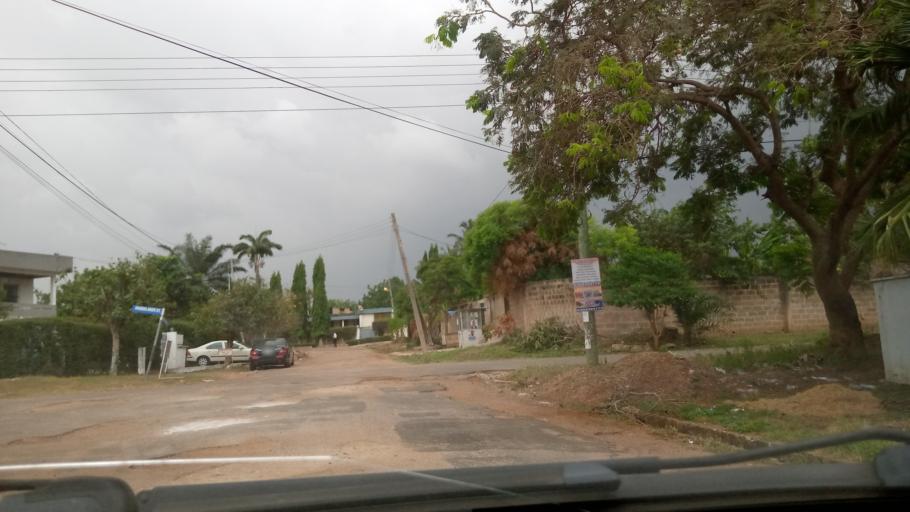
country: GH
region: Greater Accra
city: Dome
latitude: 5.6139
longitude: -0.2069
